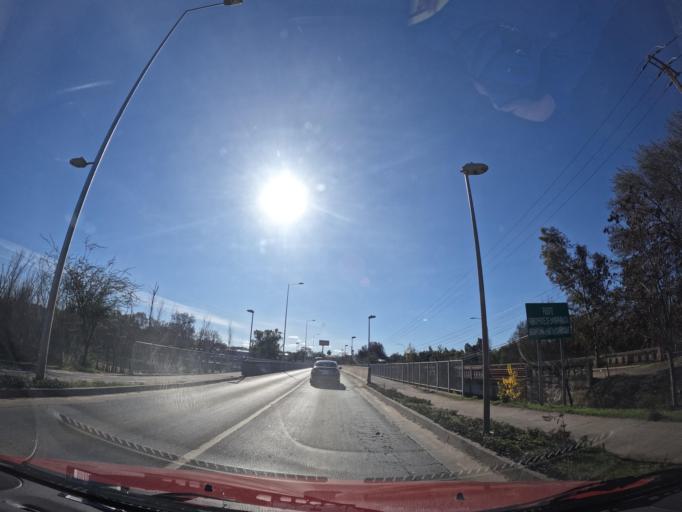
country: CL
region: Maule
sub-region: Provincia de Cauquenes
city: Cauquenes
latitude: -35.9746
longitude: -72.3153
